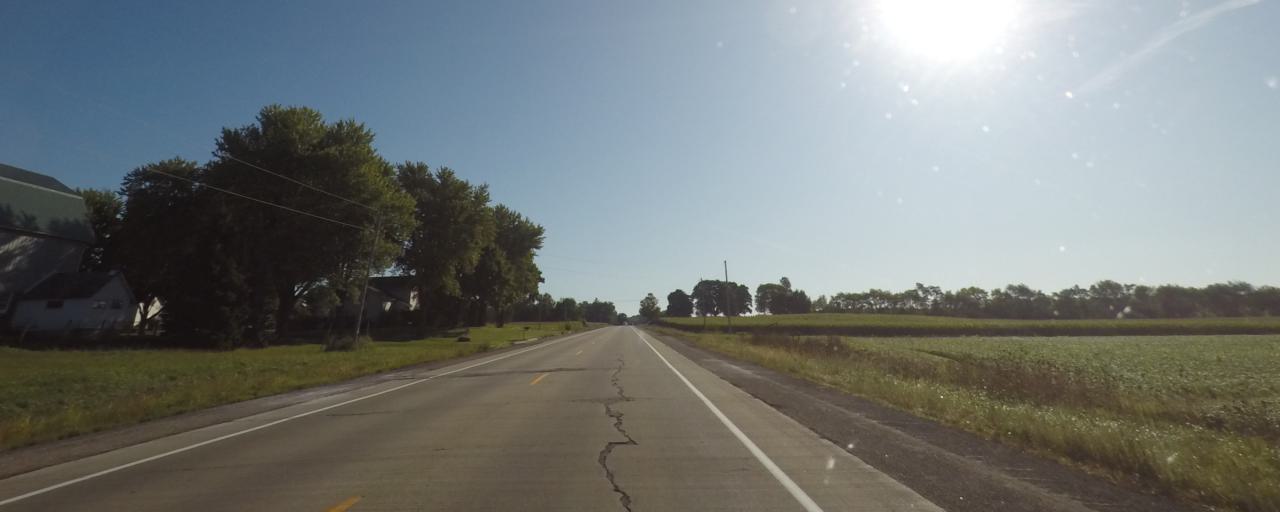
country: US
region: Wisconsin
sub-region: Dane County
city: Cottage Grove
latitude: 43.0316
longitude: -89.1441
